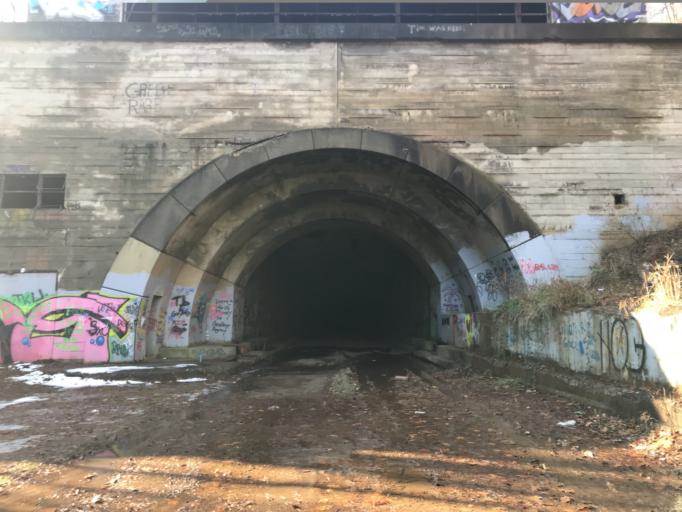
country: US
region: Pennsylvania
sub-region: Fulton County
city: McConnellsburg
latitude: 40.0474
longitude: -78.1170
